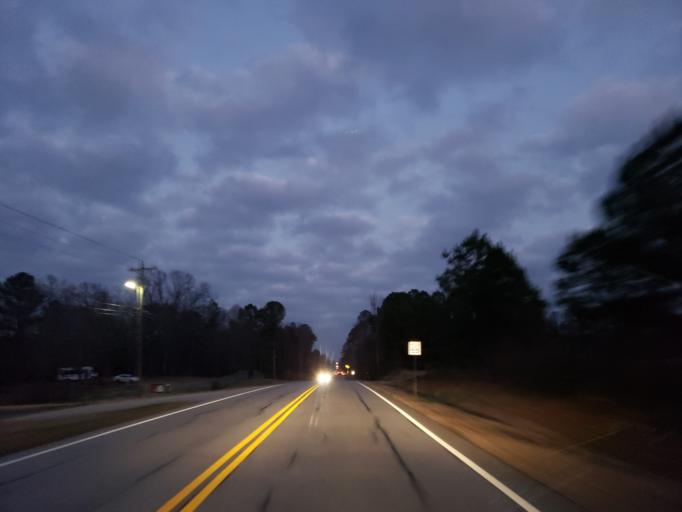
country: US
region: Georgia
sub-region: Carroll County
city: Temple
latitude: 33.8303
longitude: -85.0327
